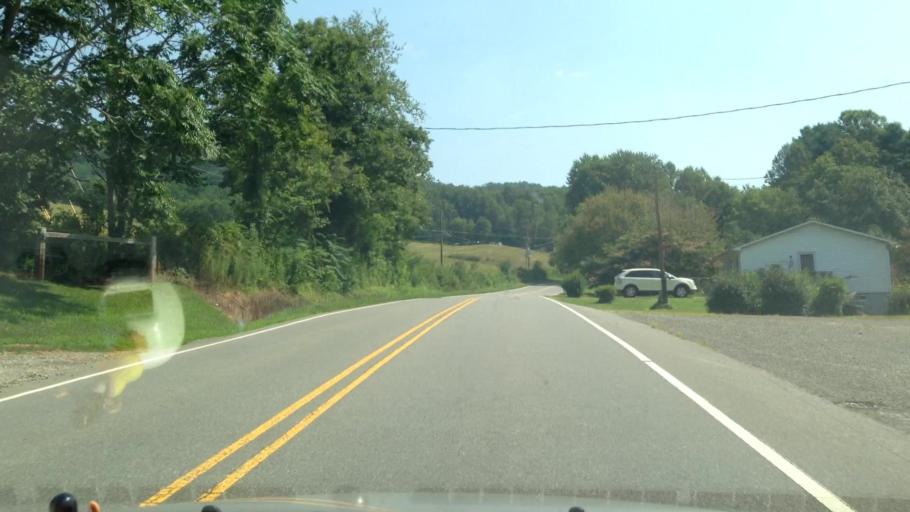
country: US
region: North Carolina
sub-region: Surry County
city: Flat Rock
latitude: 36.5301
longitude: -80.5278
